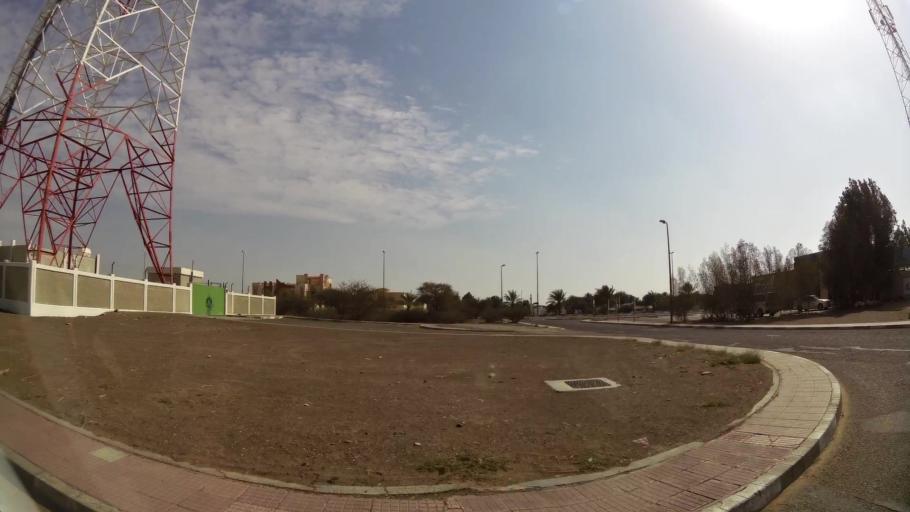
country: AE
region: Abu Dhabi
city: Al Ain
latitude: 24.0945
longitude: 55.9145
